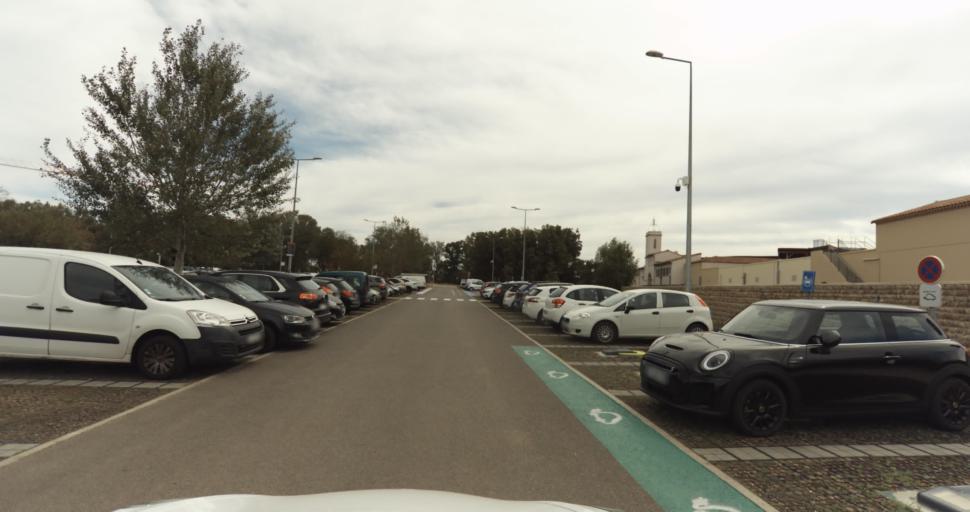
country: FR
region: Provence-Alpes-Cote d'Azur
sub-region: Departement des Bouches-du-Rhone
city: Miramas
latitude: 43.5953
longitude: 4.9919
